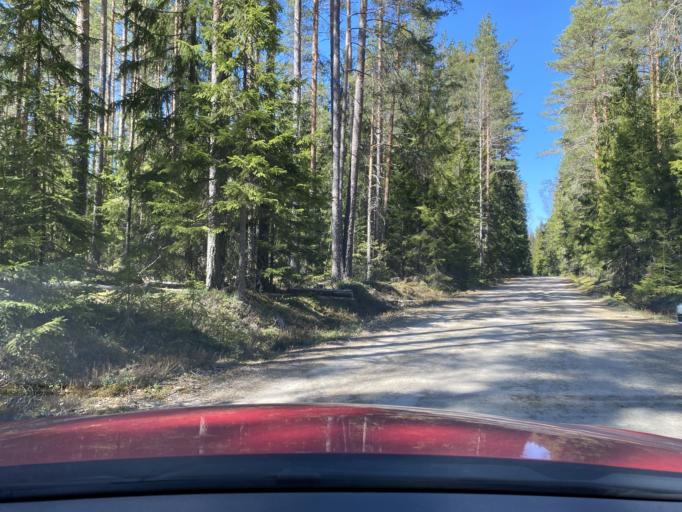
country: FI
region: Uusimaa
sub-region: Helsinki
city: Kaerkoelae
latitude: 60.6528
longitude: 23.8783
